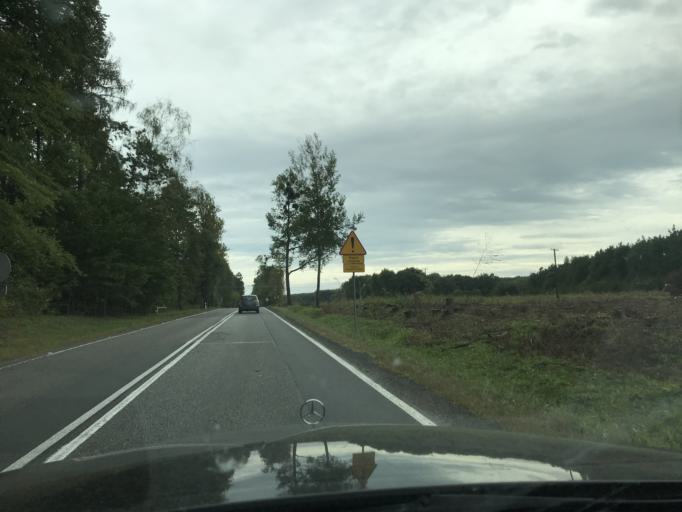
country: PL
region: Lublin Voivodeship
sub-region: Powiat krasnicki
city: Szastarka
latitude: 50.8618
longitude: 22.2789
